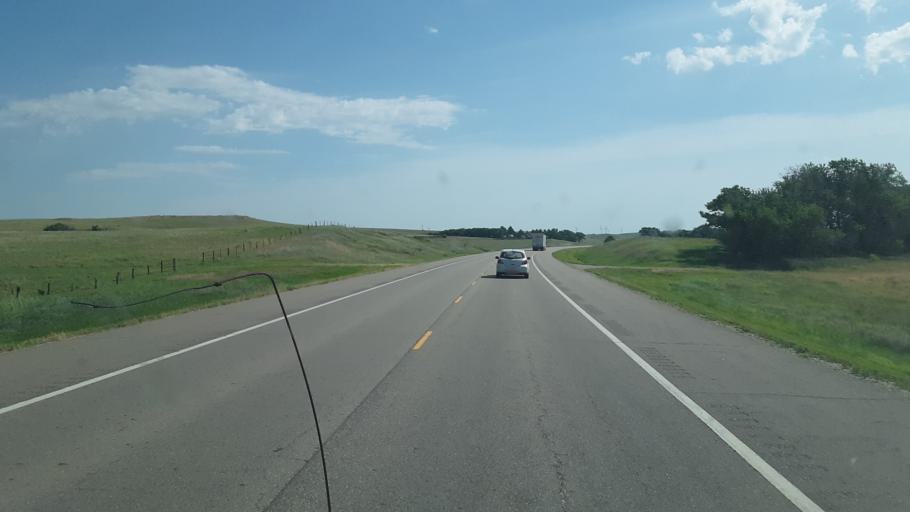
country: US
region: Kansas
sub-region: Ellsworth County
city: Ellsworth
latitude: 38.8314
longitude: -98.1268
